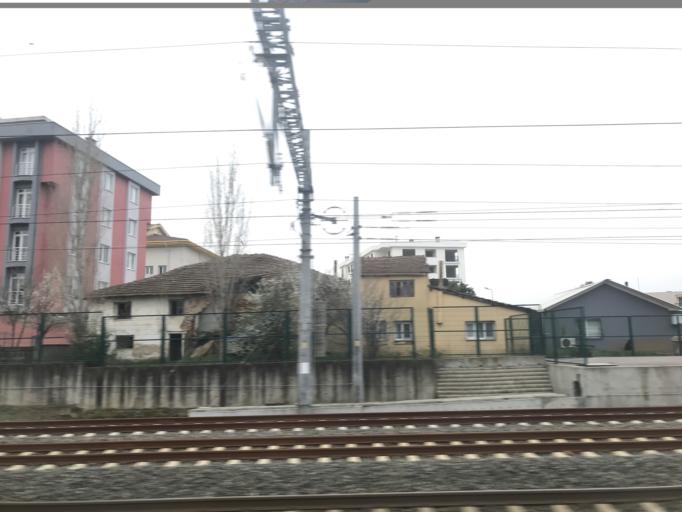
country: TR
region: Istanbul
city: Icmeler
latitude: 40.8313
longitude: 29.3207
